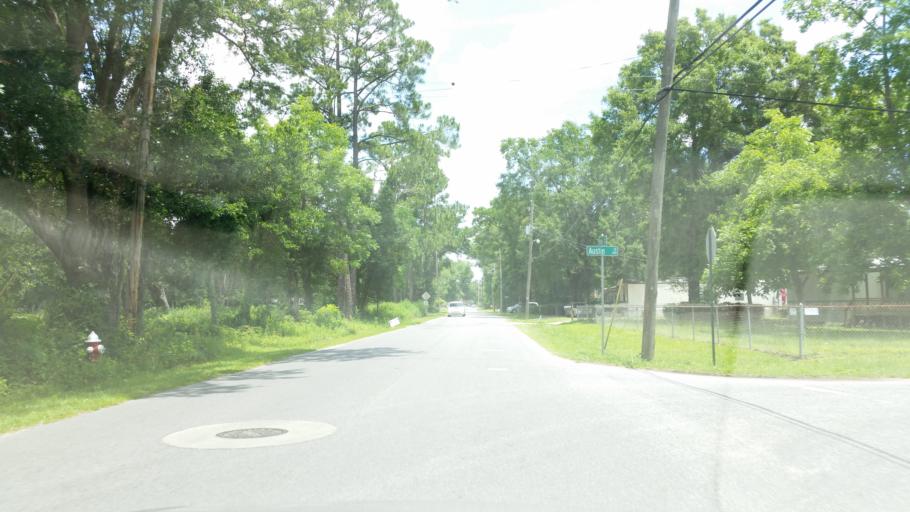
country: US
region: Florida
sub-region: Escambia County
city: Ensley
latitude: 30.5153
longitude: -87.2678
